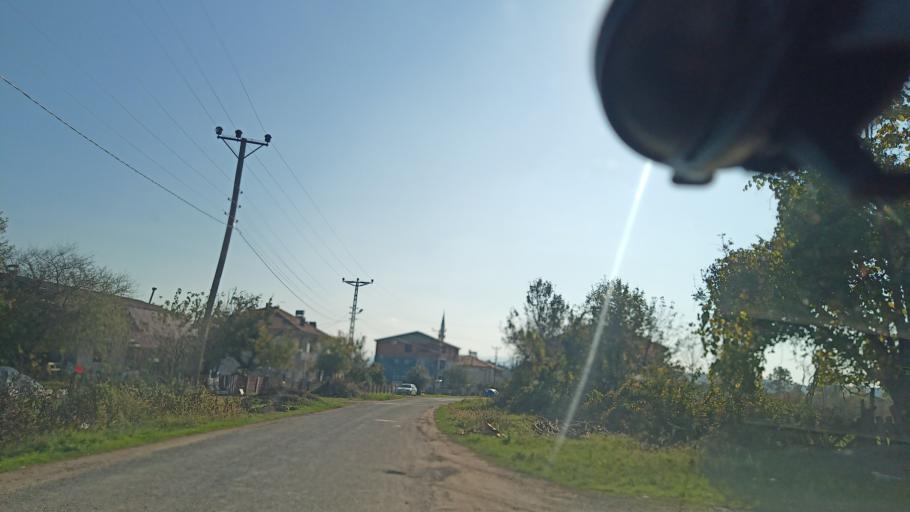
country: TR
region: Sakarya
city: Karasu
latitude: 41.0728
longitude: 30.8020
